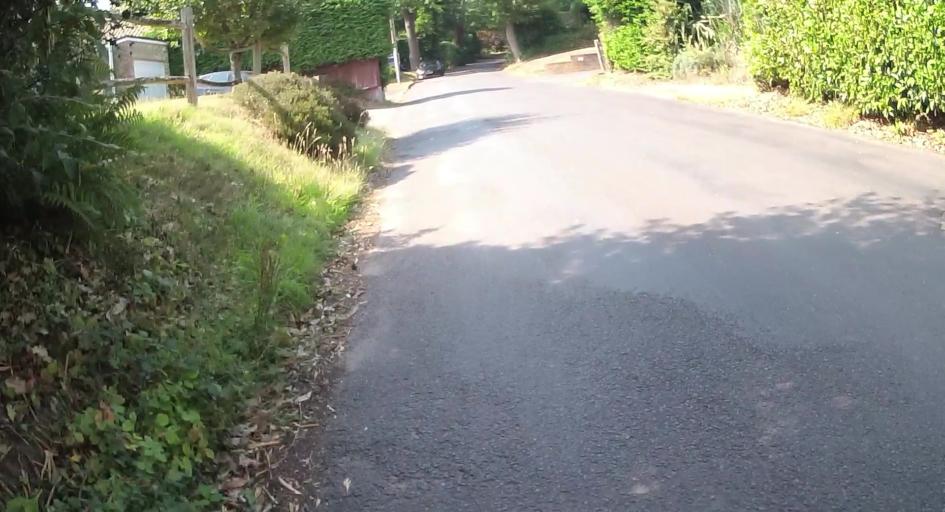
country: GB
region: England
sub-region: Surrey
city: Farnham
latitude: 51.1975
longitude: -0.8050
